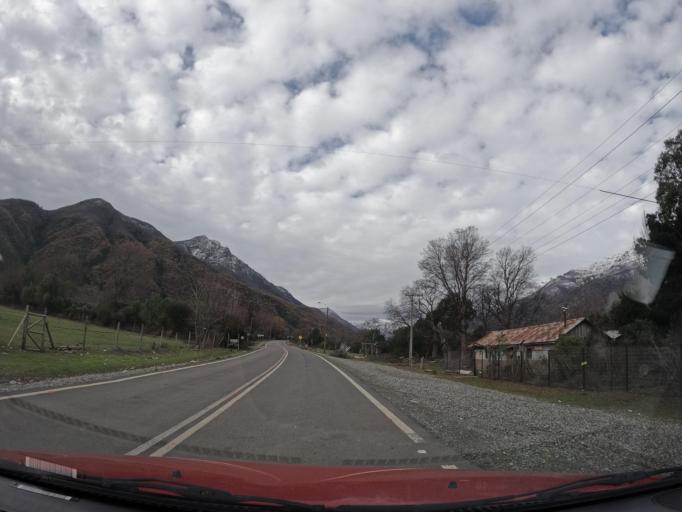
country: CL
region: Maule
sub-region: Provincia de Linares
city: Colbun
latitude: -35.8609
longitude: -71.2550
